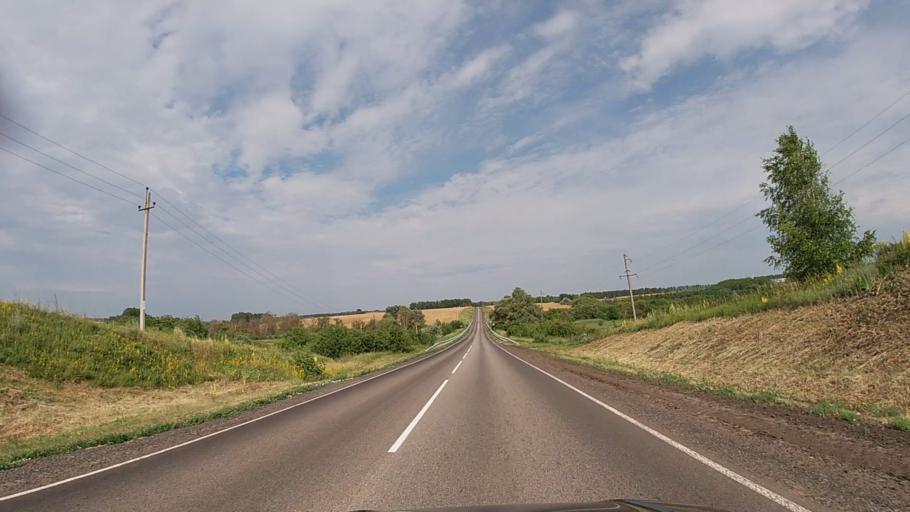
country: RU
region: Belgorod
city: Krasnaya Yaruga
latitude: 50.7990
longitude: 35.5738
